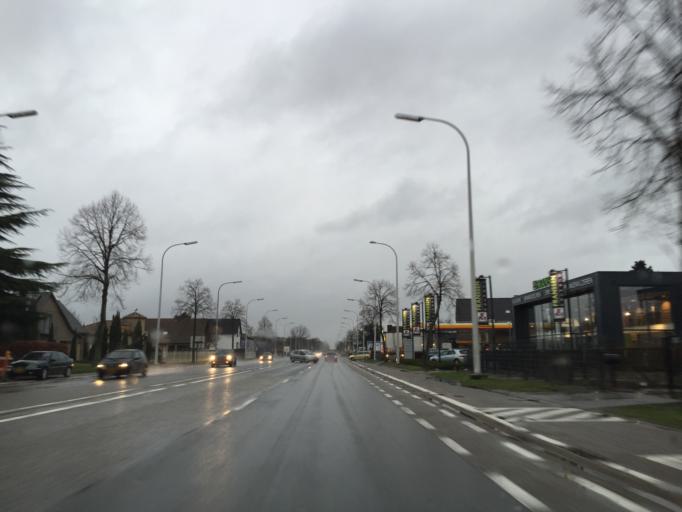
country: BE
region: Flanders
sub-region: Provincie Limburg
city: Maasmechelen
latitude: 50.9440
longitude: 5.6927
